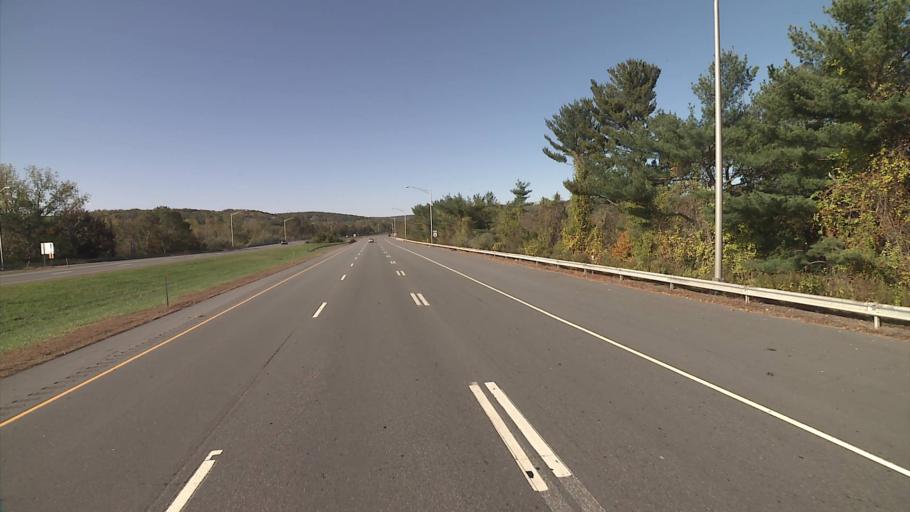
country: US
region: Connecticut
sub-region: Windham County
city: Willimantic
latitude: 41.7258
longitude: -72.2442
